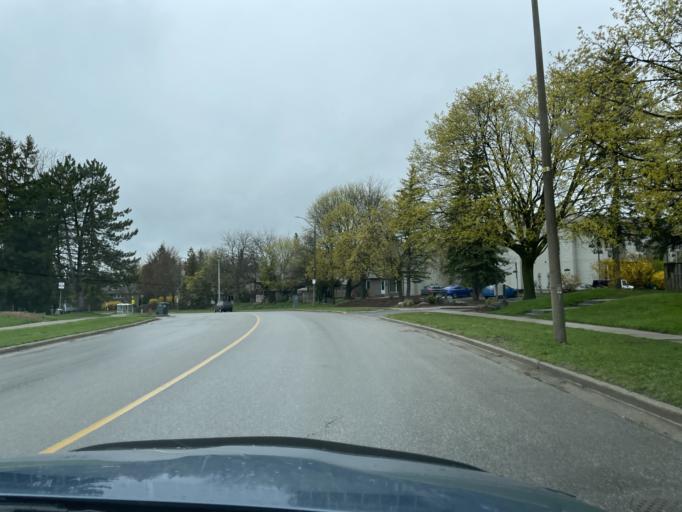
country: CA
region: Ontario
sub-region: Wellington County
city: Guelph
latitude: 43.5199
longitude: -80.2390
